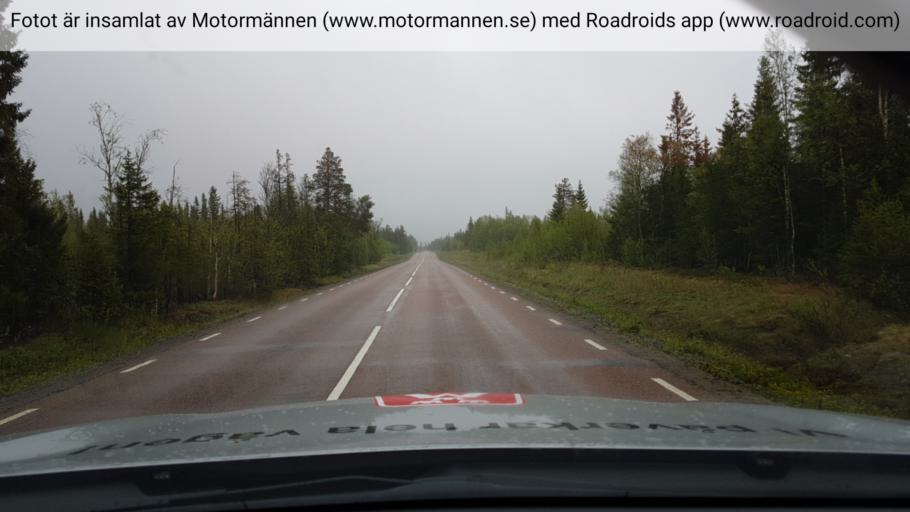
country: SE
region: Jaemtland
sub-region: Krokoms Kommun
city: Valla
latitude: 63.1358
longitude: 13.9359
